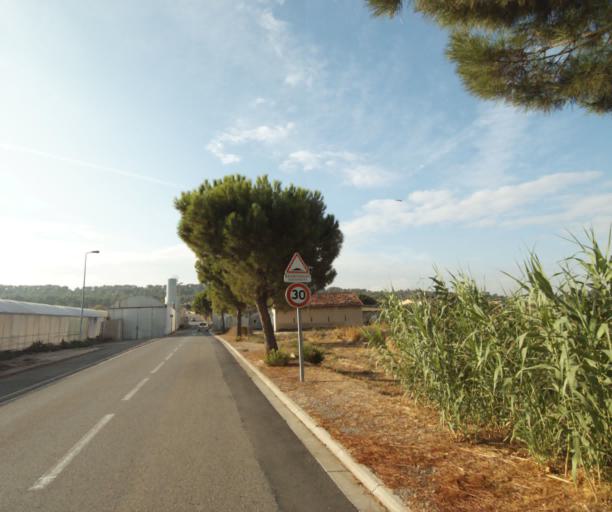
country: FR
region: Provence-Alpes-Cote d'Azur
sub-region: Departement des Bouches-du-Rhone
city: Saint-Victoret
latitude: 43.4158
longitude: 5.2653
